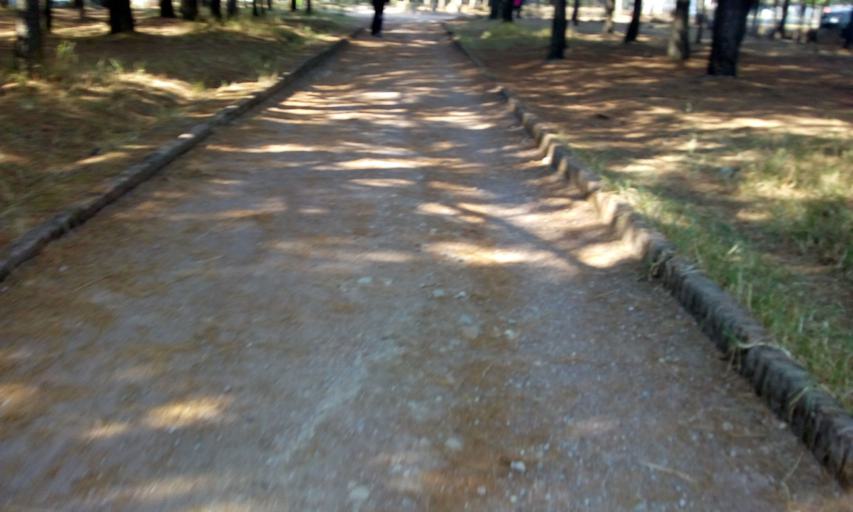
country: MX
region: Mexico
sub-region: Zinacantepec
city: San Jose Barbabosa
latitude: 19.2799
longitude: -99.6976
